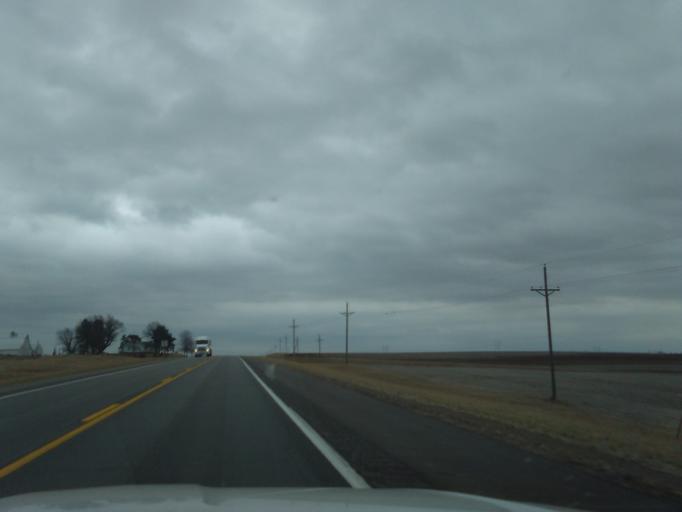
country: US
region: Nebraska
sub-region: Nemaha County
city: Auburn
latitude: 40.3927
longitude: -95.7555
